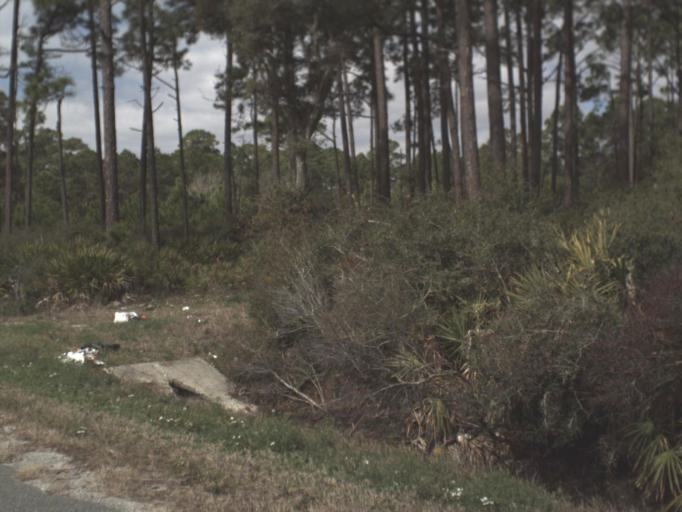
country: US
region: Florida
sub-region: Franklin County
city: Eastpoint
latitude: 29.7531
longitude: -84.8432
